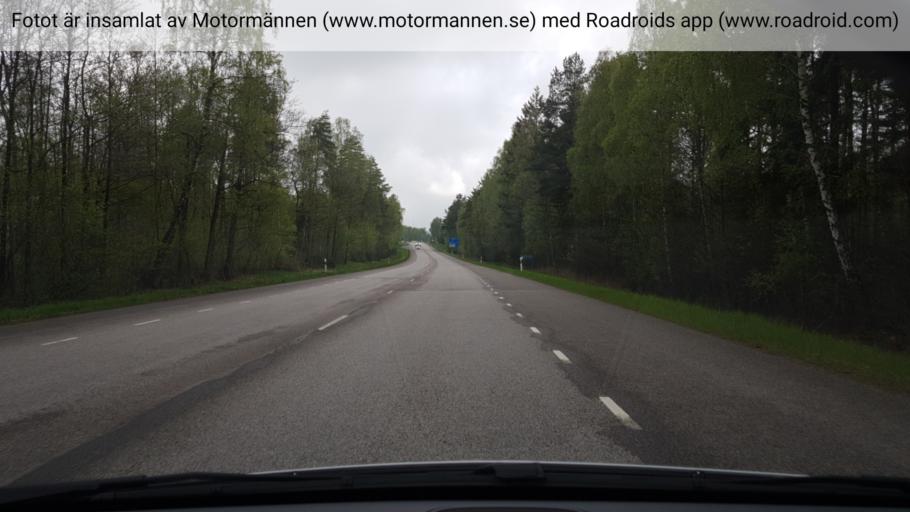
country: SE
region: Vaestra Goetaland
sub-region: Skovde Kommun
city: Stopen
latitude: 58.4228
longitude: 13.8953
